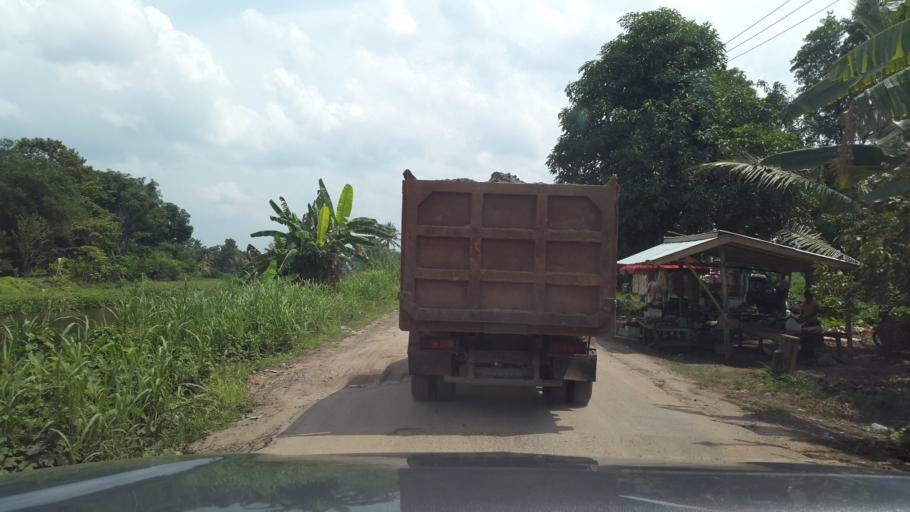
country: ID
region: South Sumatra
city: Tanjung Lubuk
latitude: -3.2667
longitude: 104.8695
